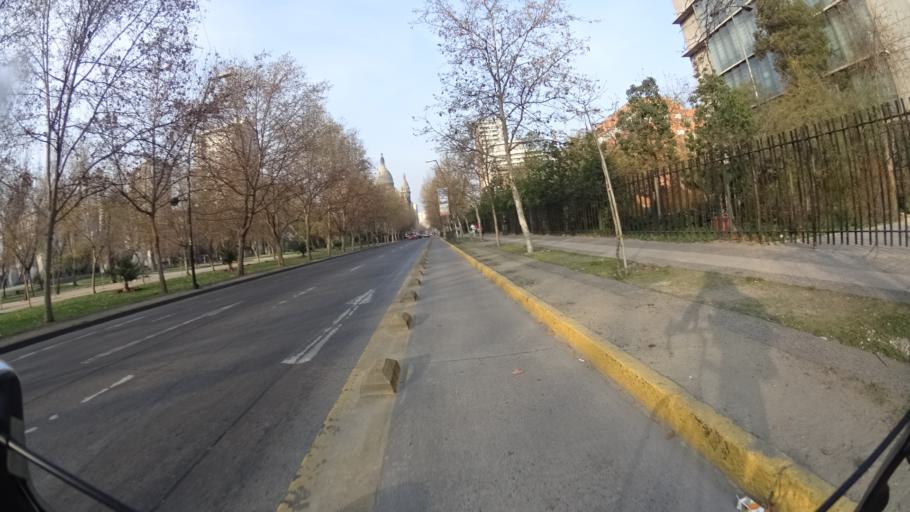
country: CL
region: Santiago Metropolitan
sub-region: Provincia de Santiago
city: Santiago
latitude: -33.4526
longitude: -70.6526
